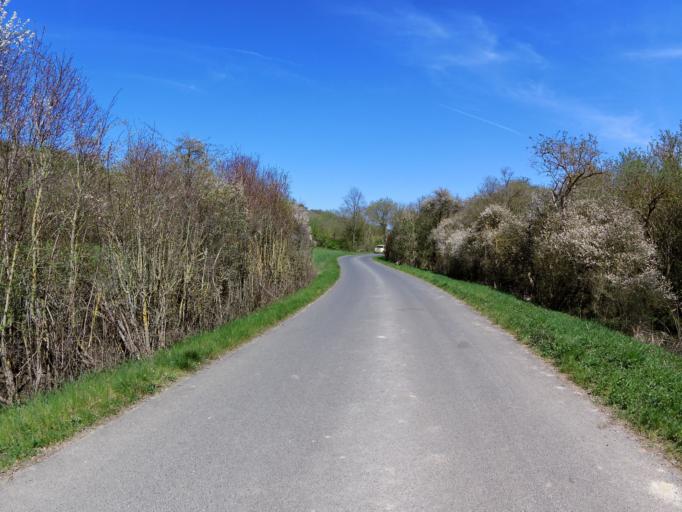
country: DE
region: Bavaria
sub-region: Regierungsbezirk Unterfranken
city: Rottendorf
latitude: 49.7952
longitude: 10.0376
